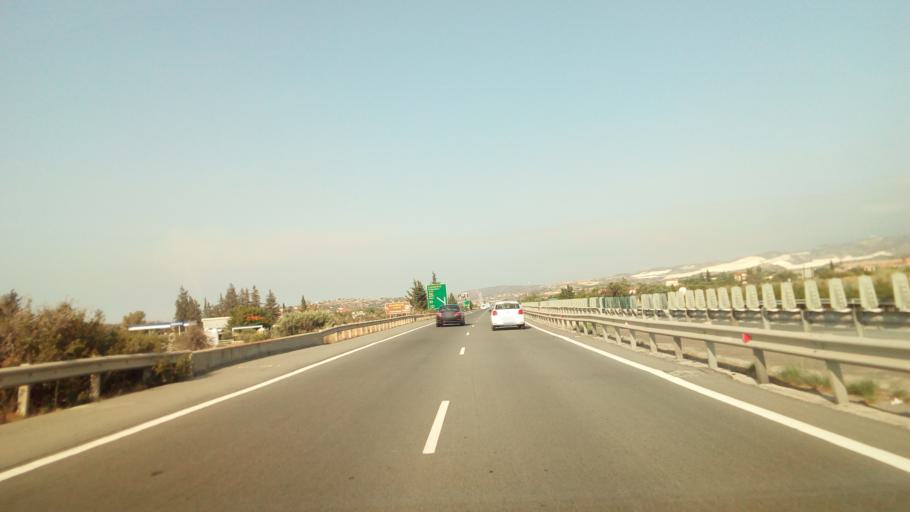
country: CY
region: Larnaka
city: Kofinou
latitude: 34.7556
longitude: 33.3184
